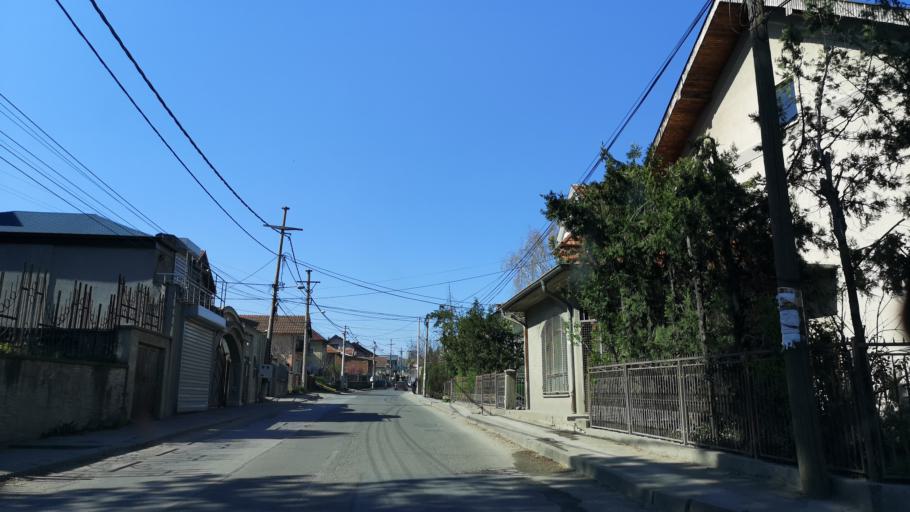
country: RS
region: Central Serbia
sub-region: Belgrade
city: Zvezdara
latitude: 44.7612
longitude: 20.5503
